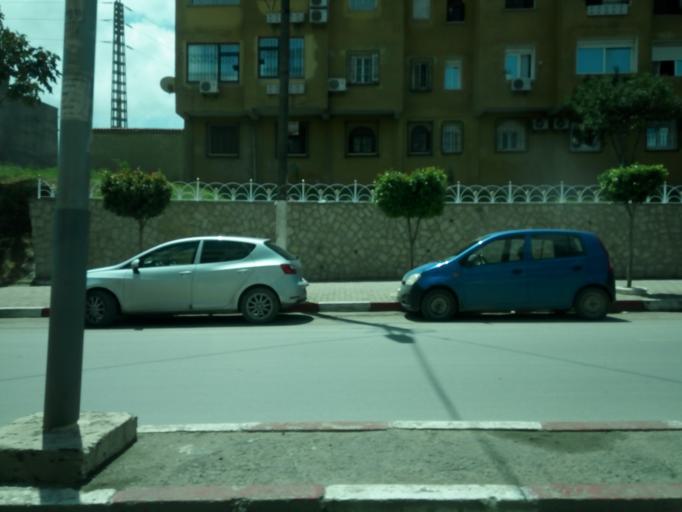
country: DZ
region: Tipaza
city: Saoula
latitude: 36.7209
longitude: 2.9940
